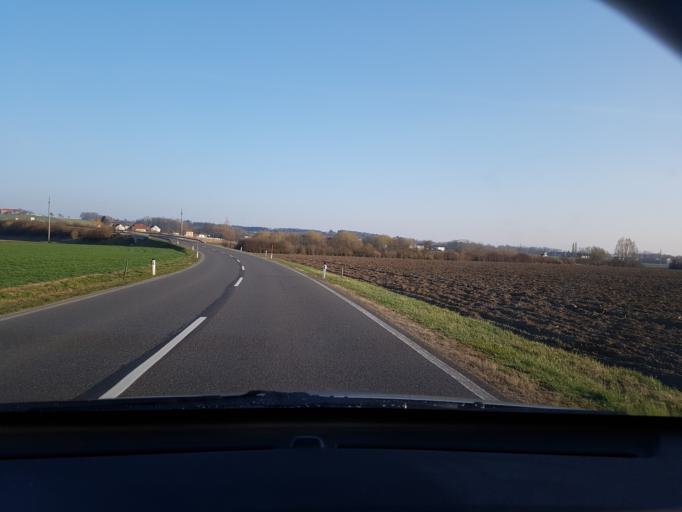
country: AT
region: Upper Austria
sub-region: Politischer Bezirk Linz-Land
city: Ansfelden
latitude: 48.1754
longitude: 14.2503
